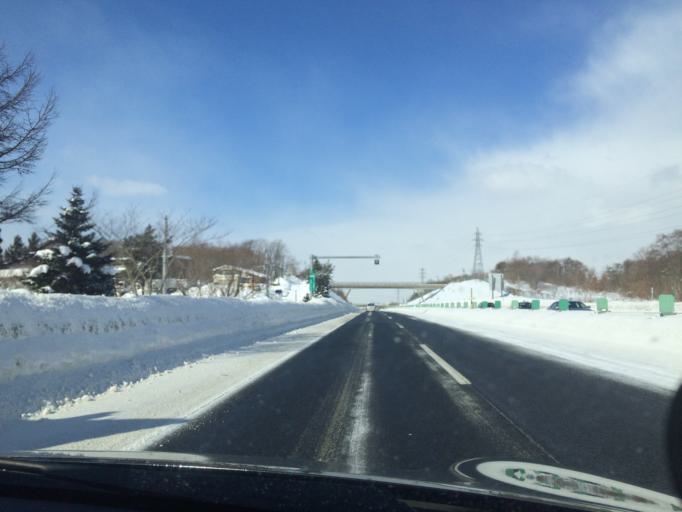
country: JP
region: Hokkaido
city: Kitahiroshima
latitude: 42.9630
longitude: 141.4974
